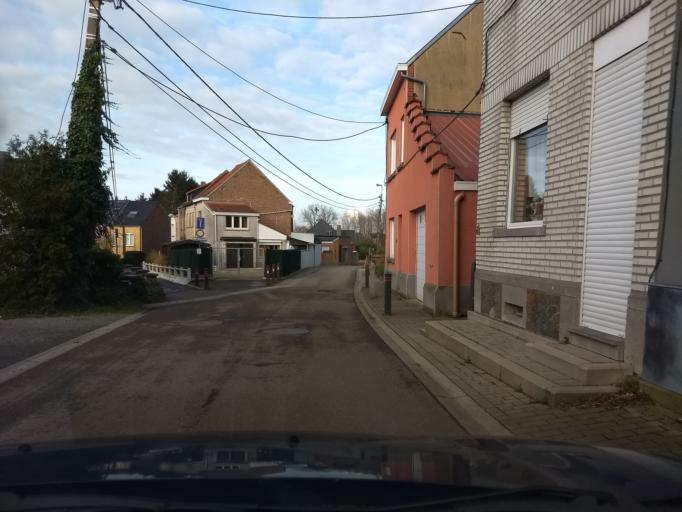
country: BE
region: Flanders
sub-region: Provincie Vlaams-Brabant
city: Halle
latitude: 50.7124
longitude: 4.2348
